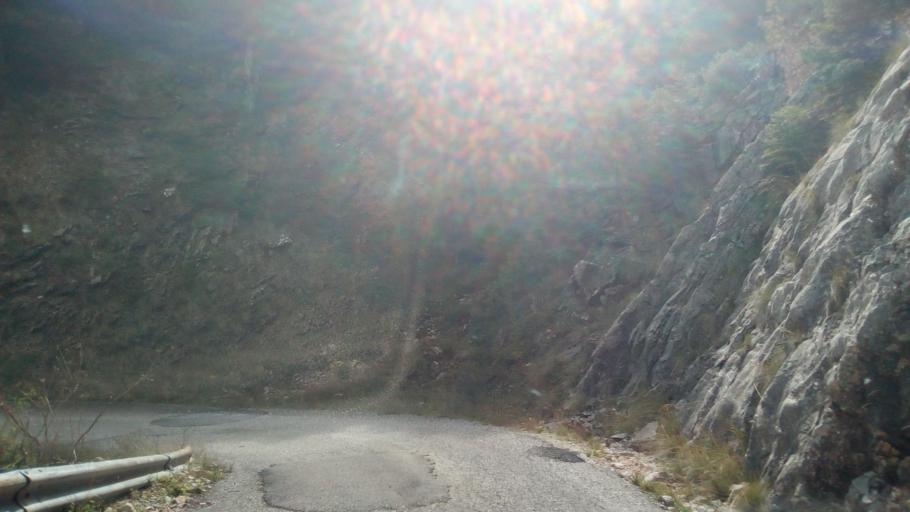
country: GR
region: West Greece
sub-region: Nomos Aitolias kai Akarnanias
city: Thermo
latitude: 38.5687
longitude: 21.8242
